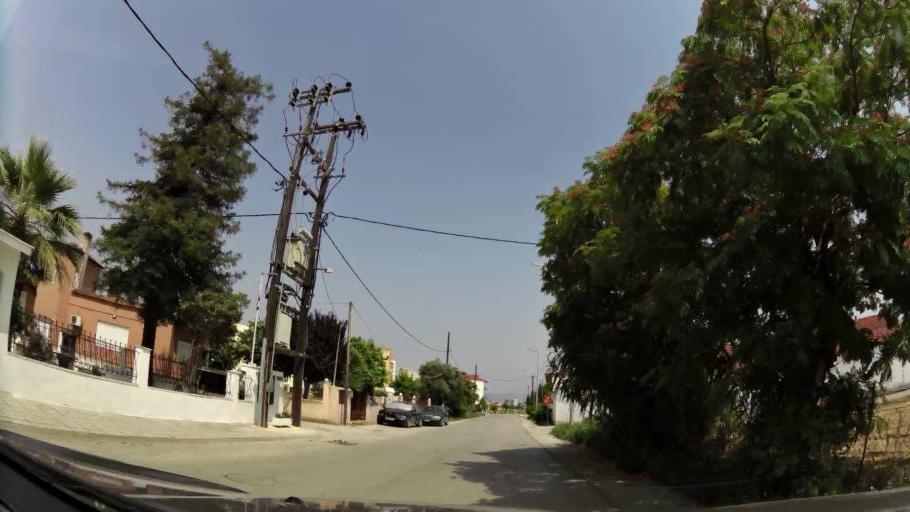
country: GR
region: Central Macedonia
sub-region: Nomos Thessalonikis
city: Nea Magnisia
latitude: 40.6861
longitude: 22.8448
